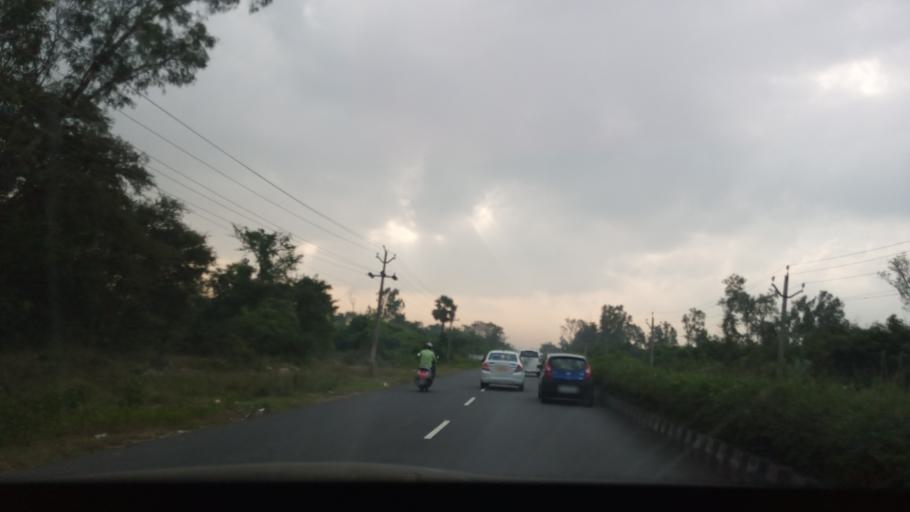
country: IN
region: Tamil Nadu
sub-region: Kancheepuram
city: Vengavasal
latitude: 12.8195
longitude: 80.1741
